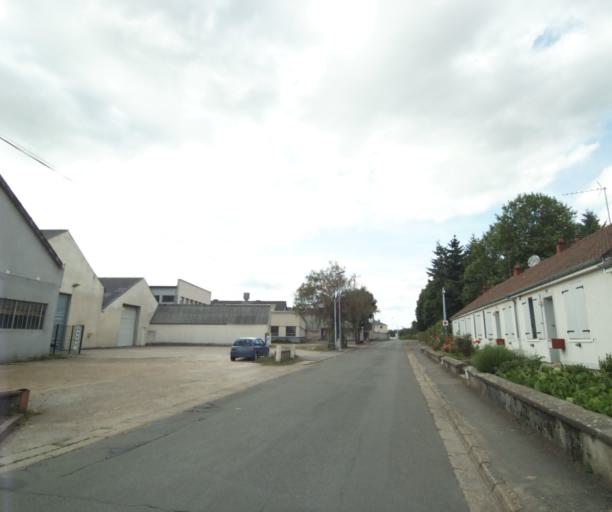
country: FR
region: Centre
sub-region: Departement d'Eure-et-Loir
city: Luisant
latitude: 48.4325
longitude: 1.4712
